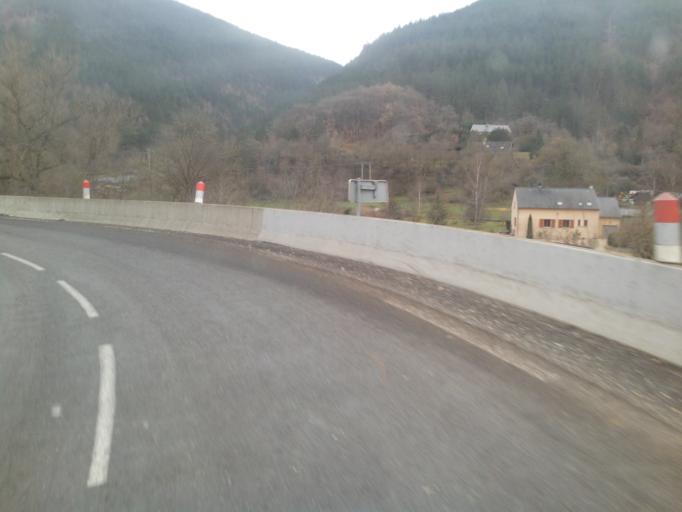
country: FR
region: Languedoc-Roussillon
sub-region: Departement de la Lozere
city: Mende
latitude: 44.4719
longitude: 3.4717
